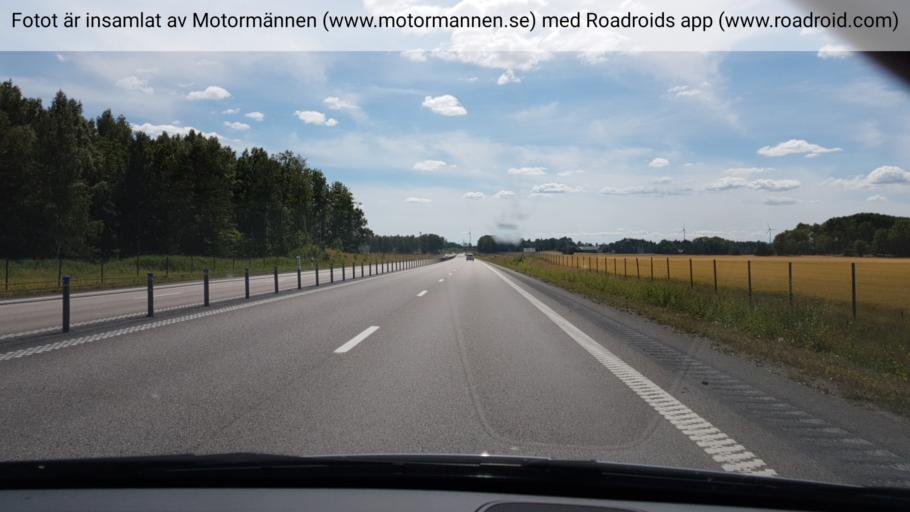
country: SE
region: Vaestra Goetaland
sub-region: Gotene Kommun
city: Goetene
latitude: 58.5176
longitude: 13.5098
